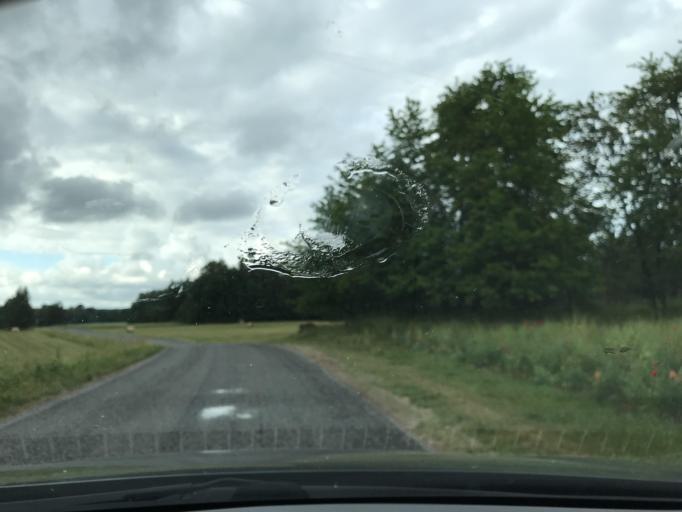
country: LV
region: Alsunga
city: Alsunga
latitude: 56.9740
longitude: 21.6405
